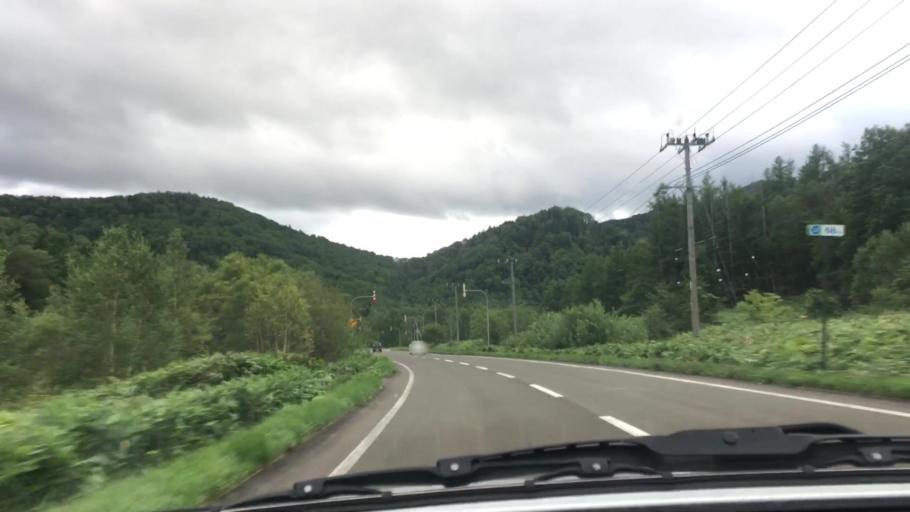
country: JP
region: Hokkaido
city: Shimo-furano
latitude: 43.0489
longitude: 142.5328
